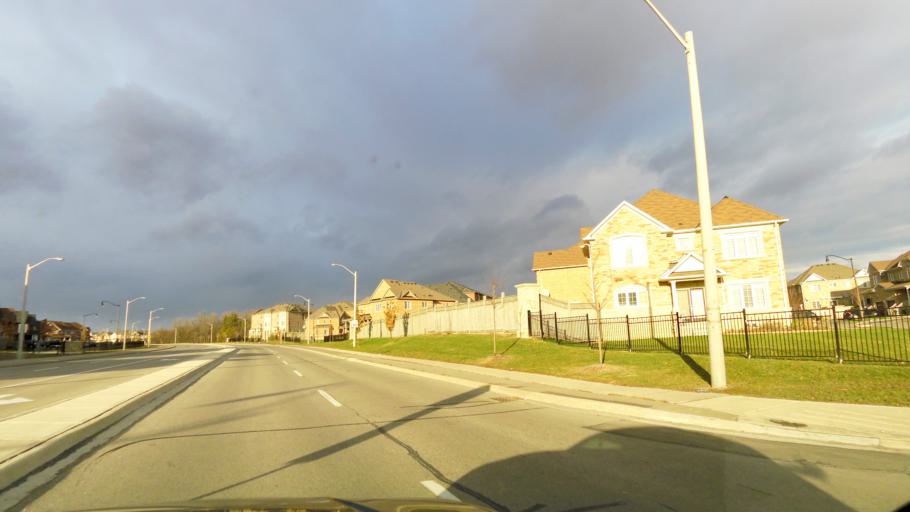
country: CA
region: Ontario
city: Brampton
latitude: 43.7882
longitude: -79.6640
